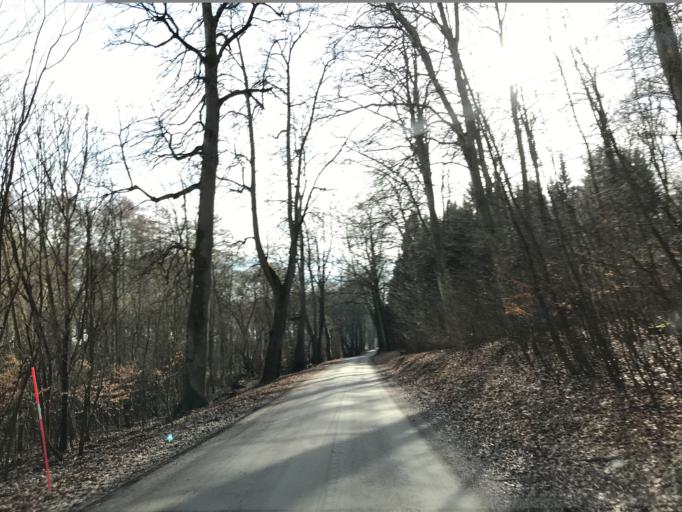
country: SE
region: Skane
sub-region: Tomelilla Kommun
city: Tomelilla
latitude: 55.5236
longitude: 13.8905
